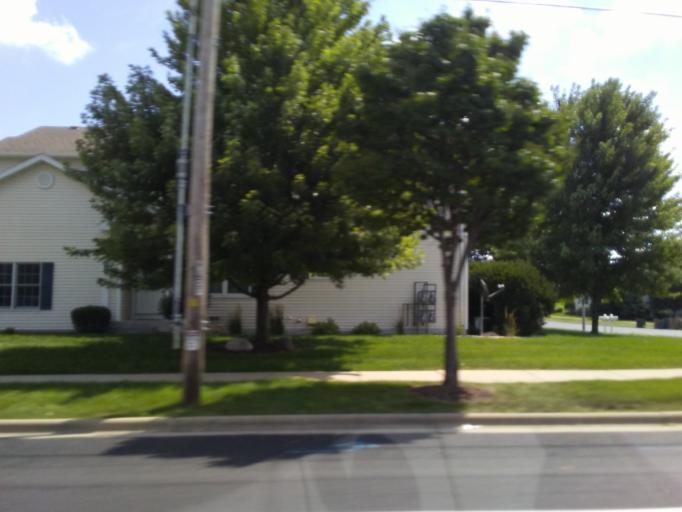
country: US
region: Wisconsin
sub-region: Dane County
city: Verona
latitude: 43.0077
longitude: -89.4990
